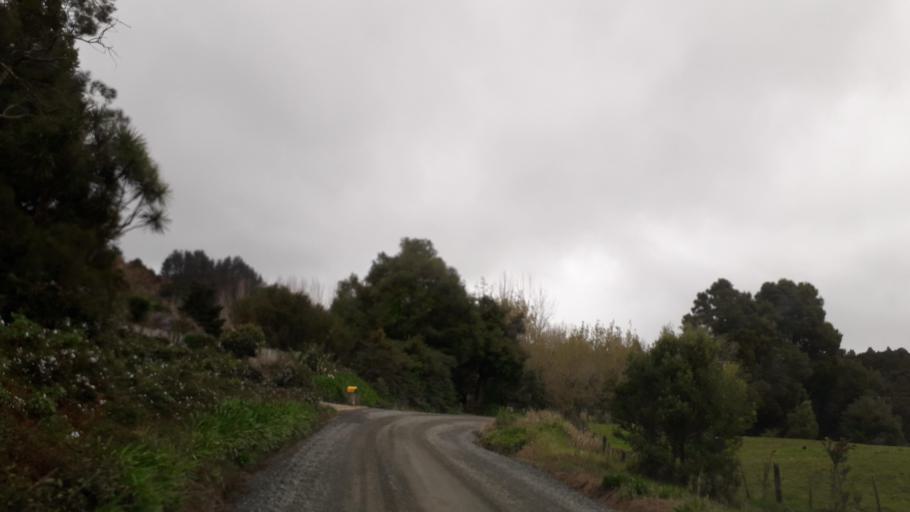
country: NZ
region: Northland
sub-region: Far North District
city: Kerikeri
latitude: -35.1198
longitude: 173.7516
